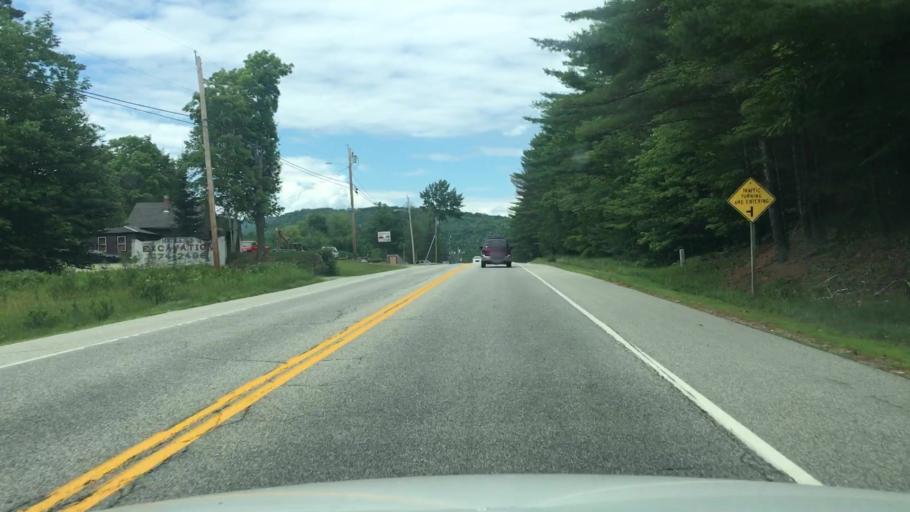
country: US
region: Maine
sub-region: Oxford County
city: West Paris
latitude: 44.3452
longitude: -70.5625
